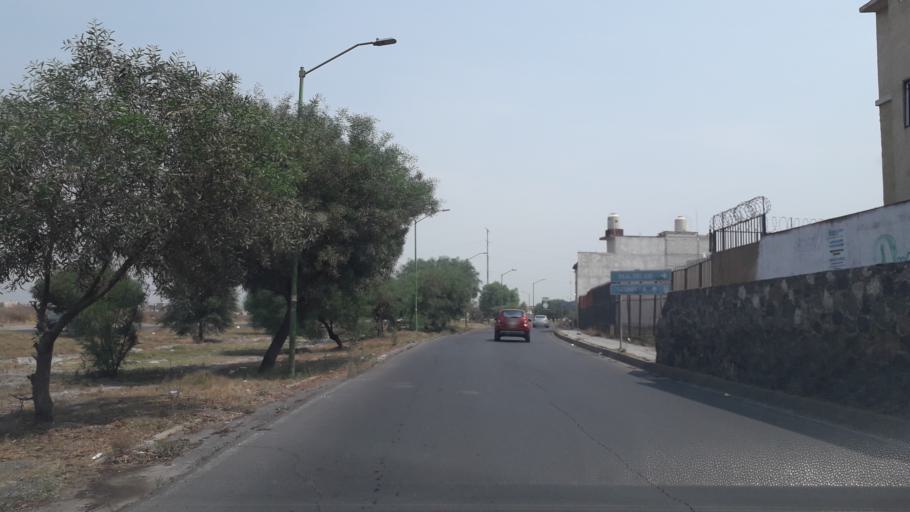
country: MX
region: Mexico
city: Santo Tomas Chiconautla
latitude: 19.6444
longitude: -99.0244
